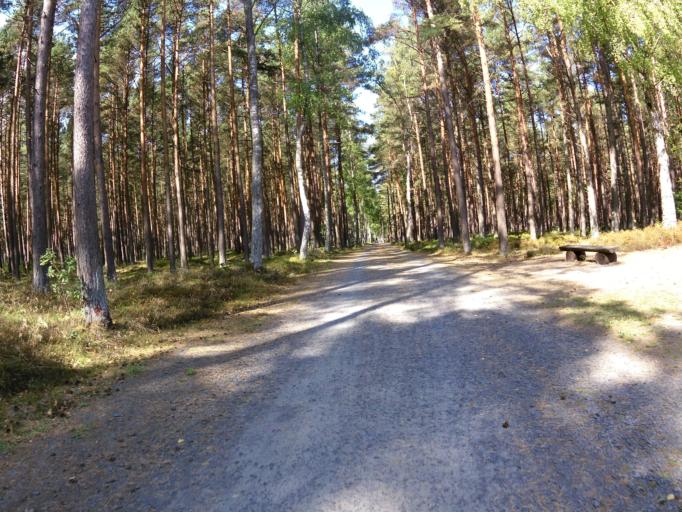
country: DE
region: Mecklenburg-Vorpommern
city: Karlshagen
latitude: 54.0945
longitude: 13.8710
